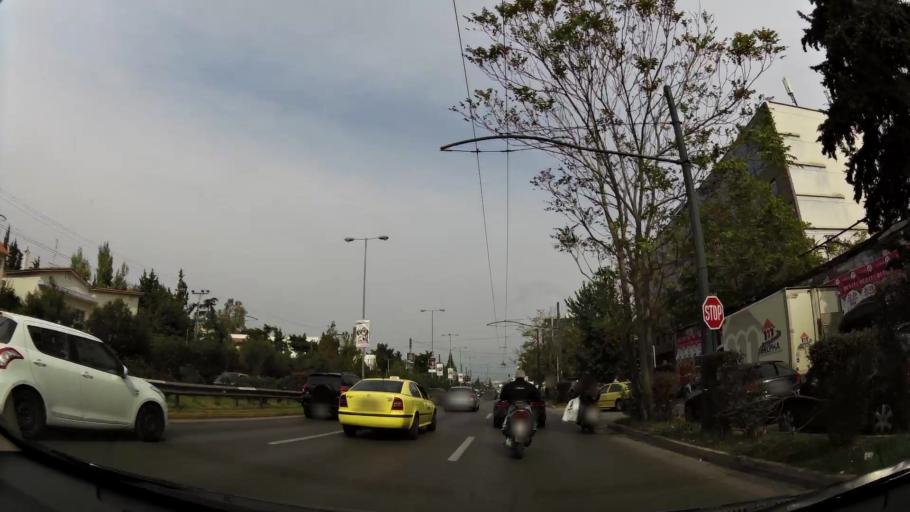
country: GR
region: Attica
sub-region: Nomarchia Athinas
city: Neo Psychiko
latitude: 38.0088
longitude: 23.7790
